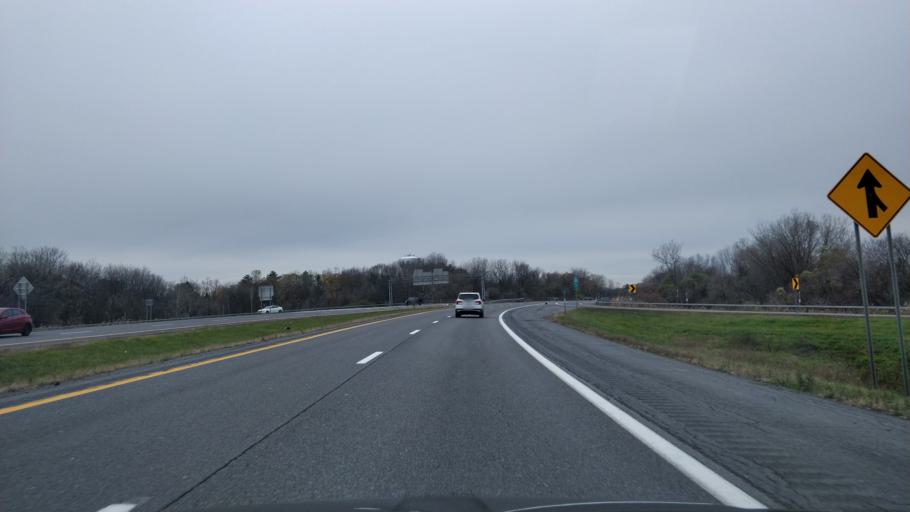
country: US
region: New York
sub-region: Onondaga County
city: North Syracuse
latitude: 43.1419
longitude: -76.1154
